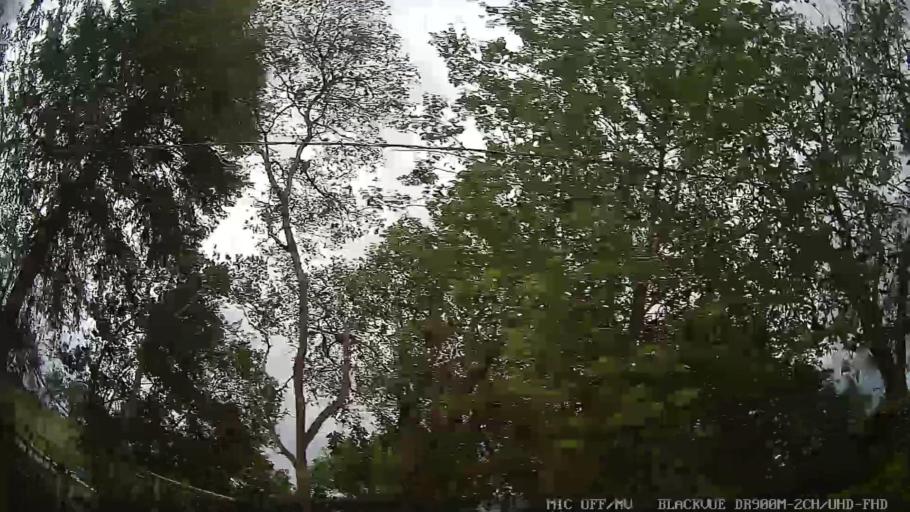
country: BR
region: Sao Paulo
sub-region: Braganca Paulista
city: Braganca Paulista
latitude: -22.9121
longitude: -46.5202
